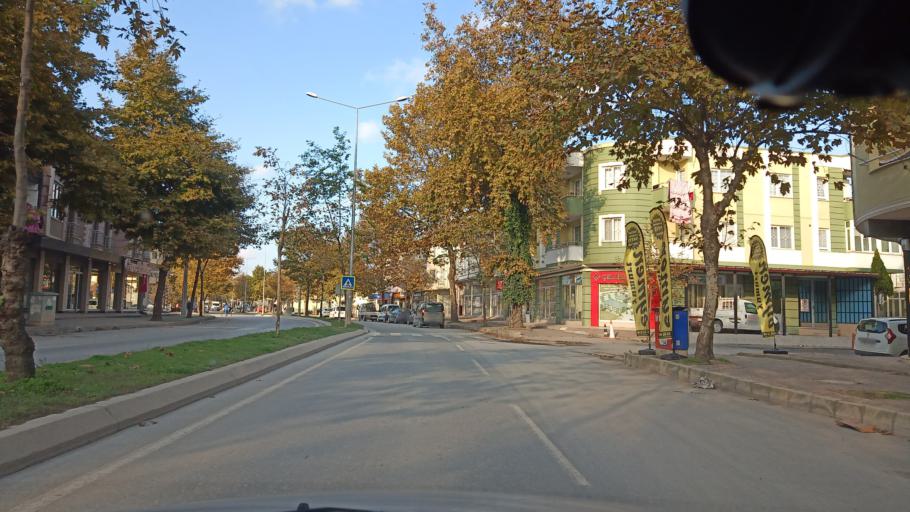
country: TR
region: Sakarya
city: Karasu
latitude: 41.1017
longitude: 30.6901
